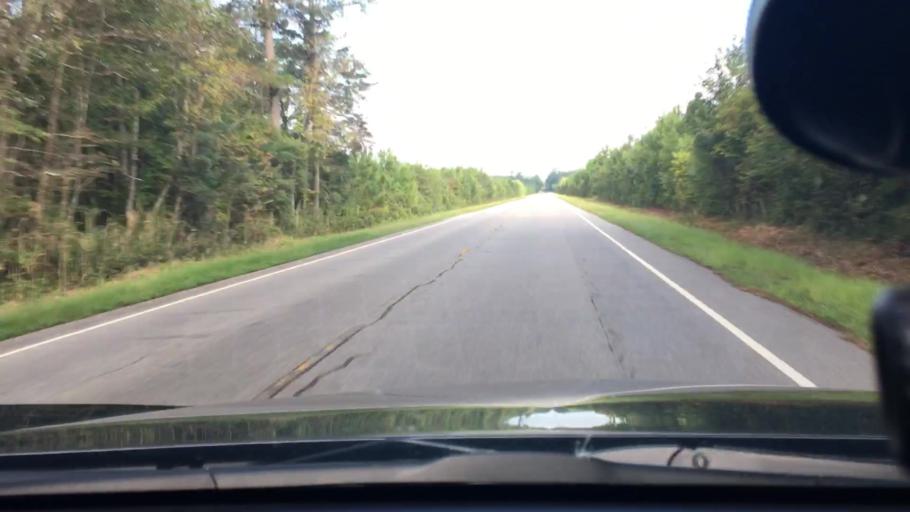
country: US
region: North Carolina
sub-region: Edgecombe County
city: Pinetops
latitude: 35.7691
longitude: -77.5686
